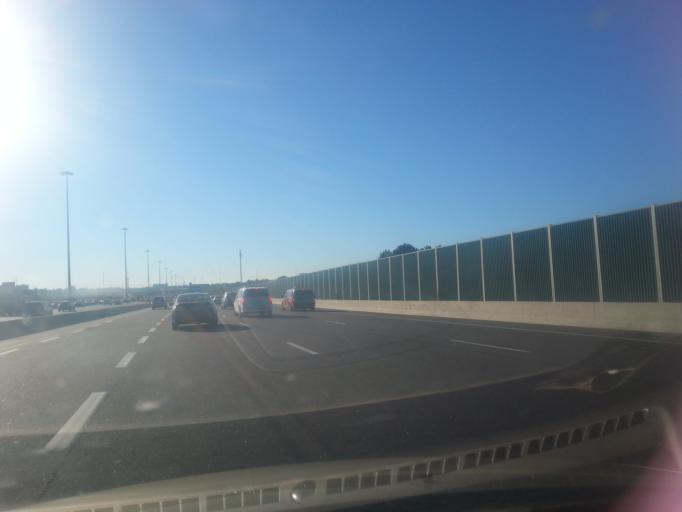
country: CA
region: Ontario
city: Concord
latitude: 43.7184
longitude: -79.5044
